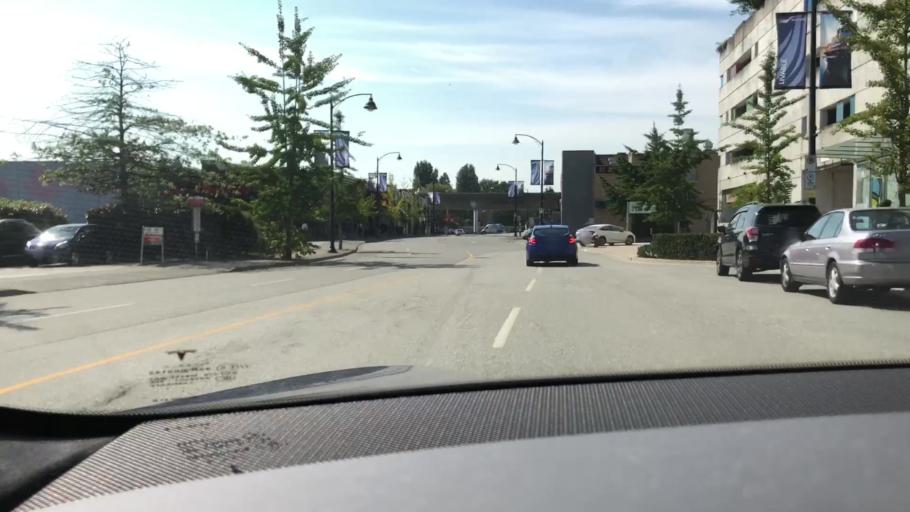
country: CA
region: British Columbia
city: Richmond
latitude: 49.1830
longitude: -123.1342
